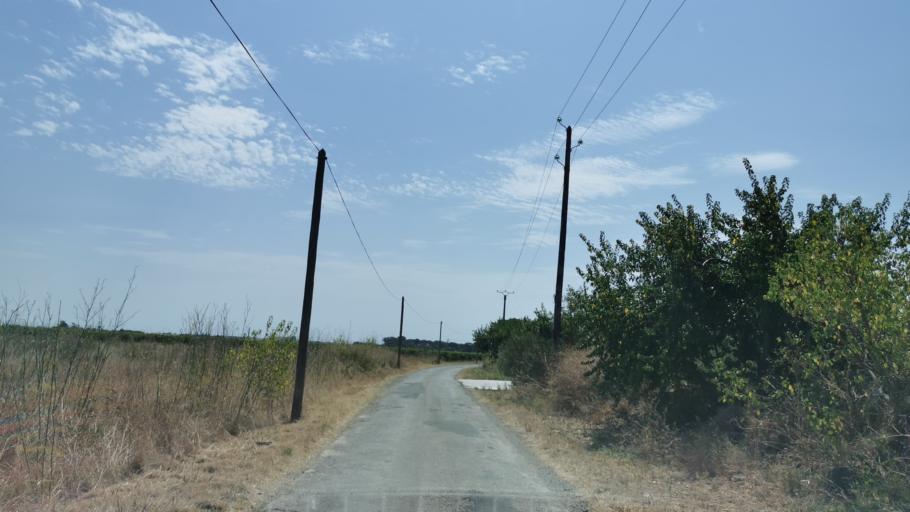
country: FR
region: Languedoc-Roussillon
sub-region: Departement de l'Aude
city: Argeliers
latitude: 43.2908
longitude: 2.8898
